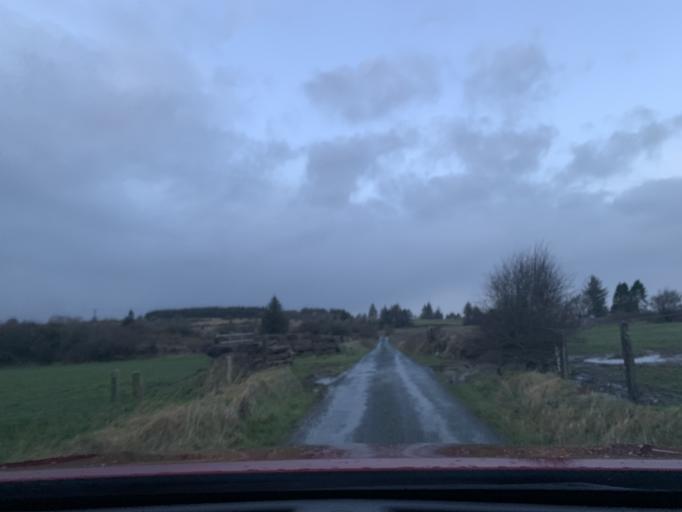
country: IE
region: Connaught
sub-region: Roscommon
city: Ballaghaderreen
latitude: 53.9706
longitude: -8.5592
